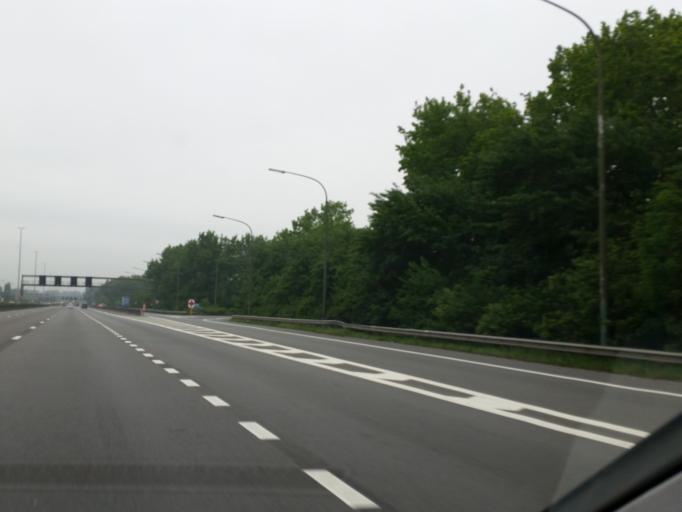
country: BE
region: Flanders
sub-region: Provincie Antwerpen
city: Antwerpen
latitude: 51.2406
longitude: 4.4264
